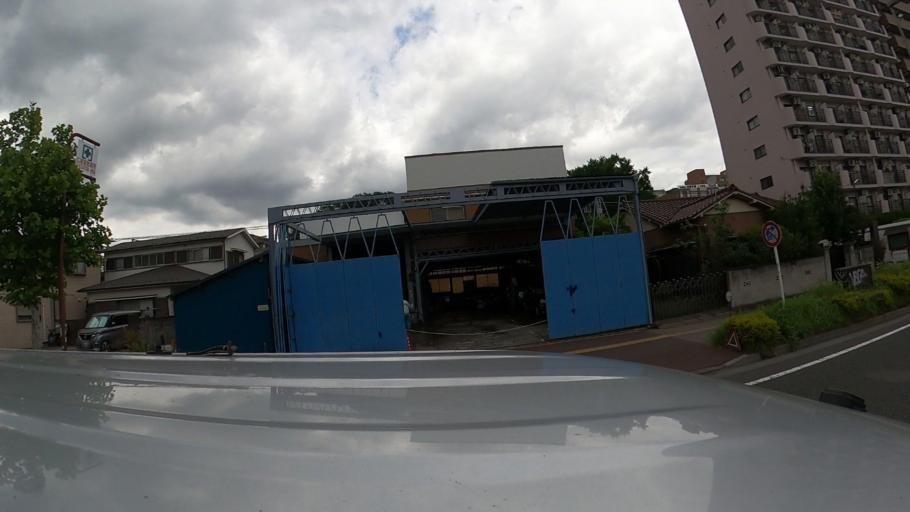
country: JP
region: Kanagawa
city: Yokohama
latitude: 35.4886
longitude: 139.6589
